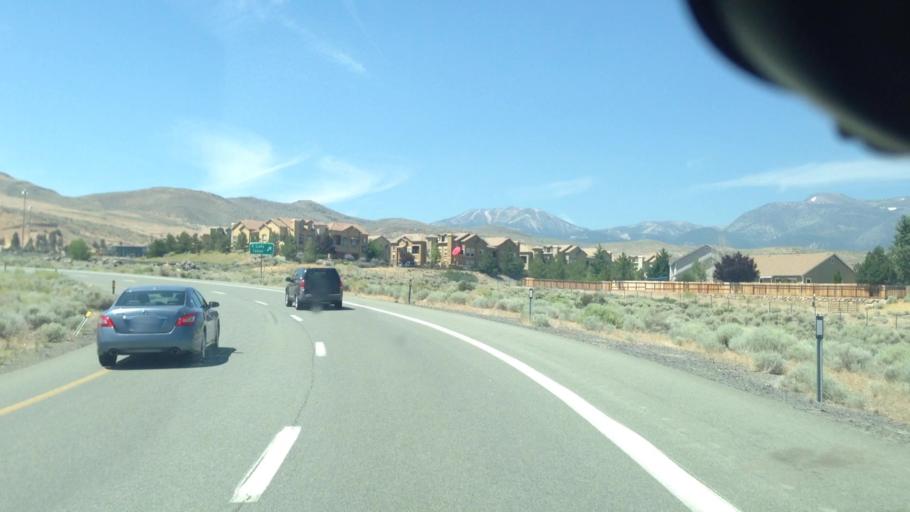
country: US
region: Nevada
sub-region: Washoe County
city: Sparks
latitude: 39.3983
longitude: -119.7603
